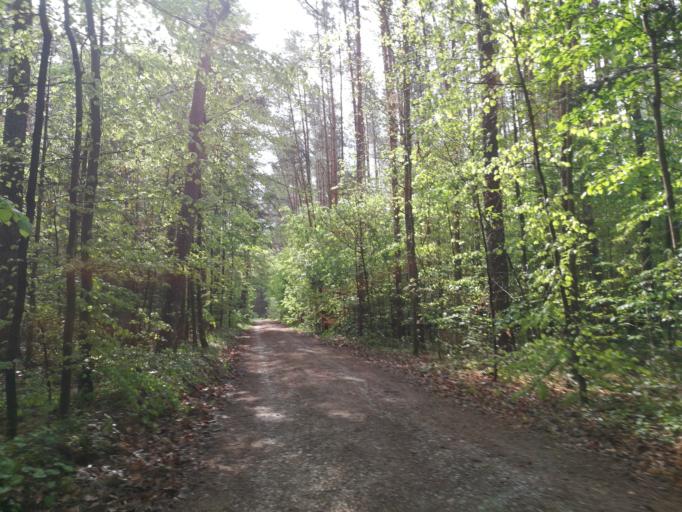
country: DE
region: Bavaria
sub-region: Regierungsbezirk Mittelfranken
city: Seukendorf
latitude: 49.4757
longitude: 10.8999
